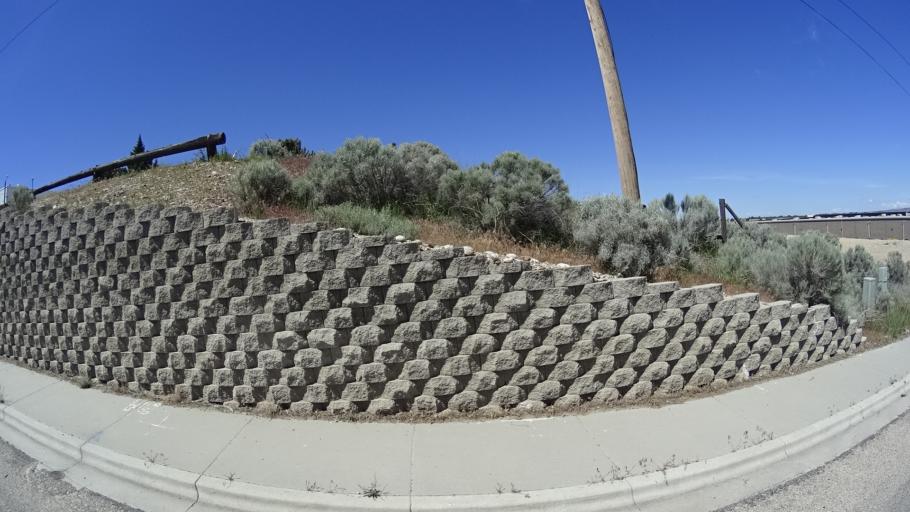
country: US
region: Idaho
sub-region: Ada County
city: Boise
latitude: 43.5658
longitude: -116.1835
